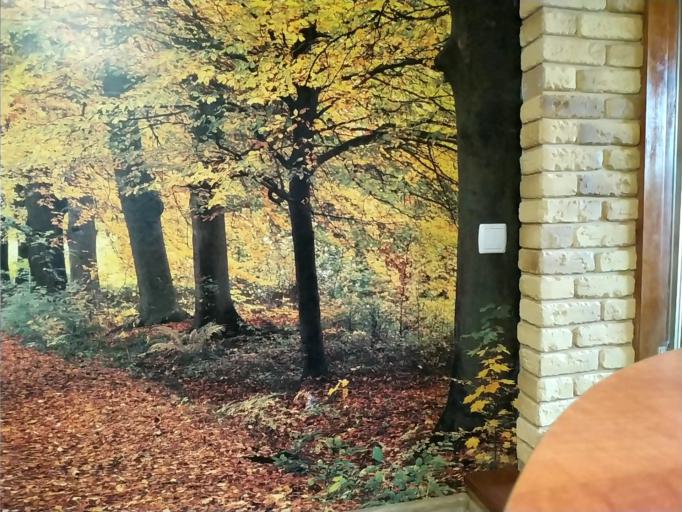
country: RU
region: Leningrad
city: Tolmachevo
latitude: 58.9380
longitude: 29.6854
